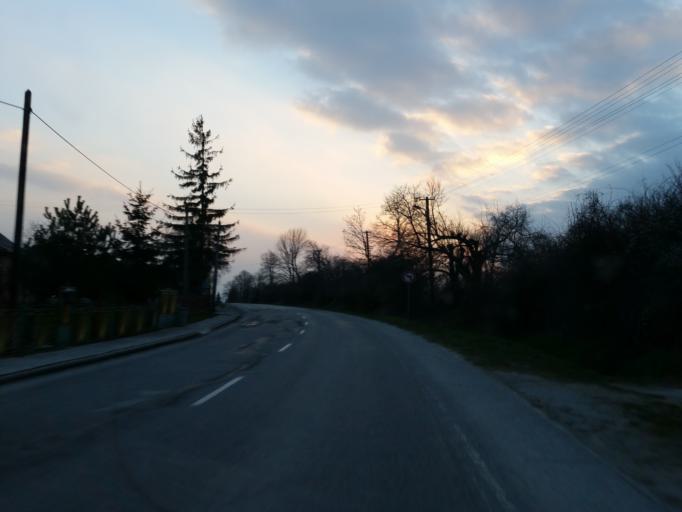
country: SK
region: Trnavsky
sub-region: Okres Trnava
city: Piestany
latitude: 48.5717
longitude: 18.0187
